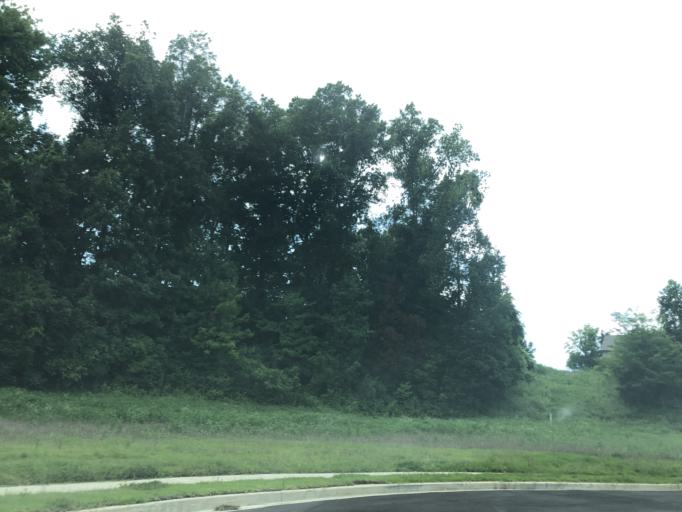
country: US
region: Tennessee
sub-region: Wilson County
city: Green Hill
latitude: 36.2112
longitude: -86.5851
